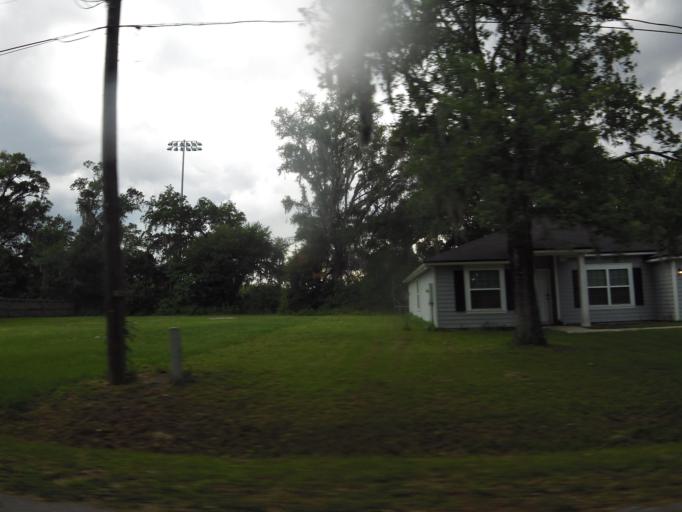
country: US
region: Florida
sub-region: Duval County
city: Jacksonville
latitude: 30.2674
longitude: -81.6350
